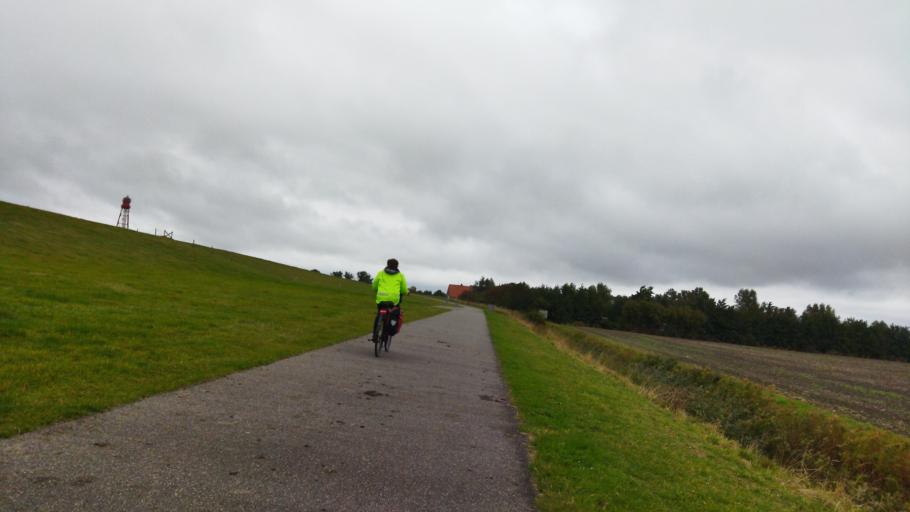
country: NL
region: Groningen
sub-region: Gemeente Delfzijl
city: Delfzijl
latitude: 53.3993
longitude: 7.0153
